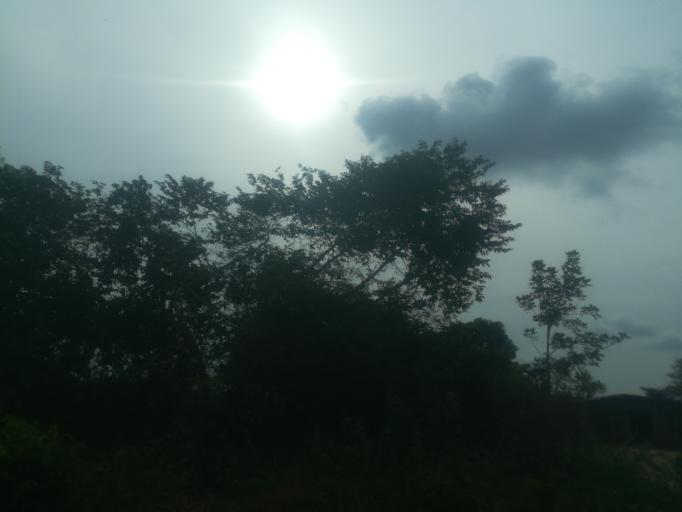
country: NG
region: Ogun
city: Ayetoro
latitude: 7.3008
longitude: 3.0757
